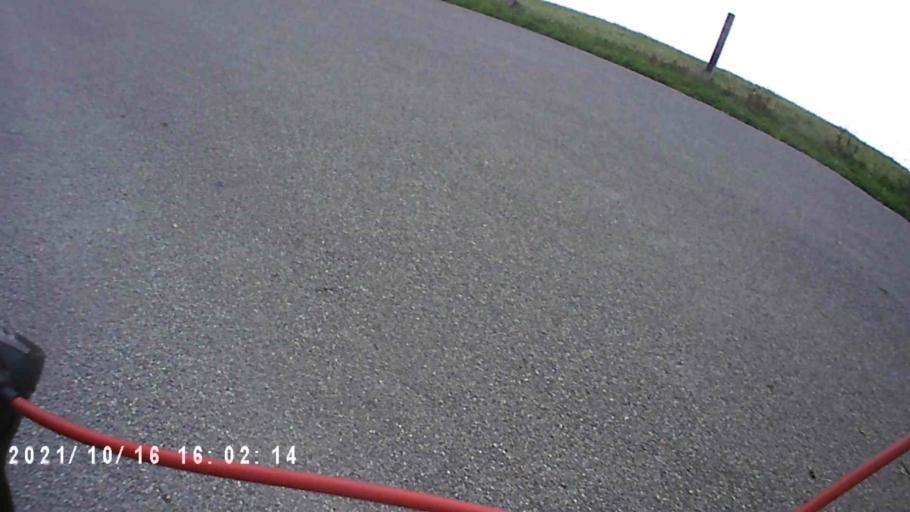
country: NL
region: Friesland
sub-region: Gemeente Dongeradeel
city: Anjum
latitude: 53.4016
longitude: 6.1302
